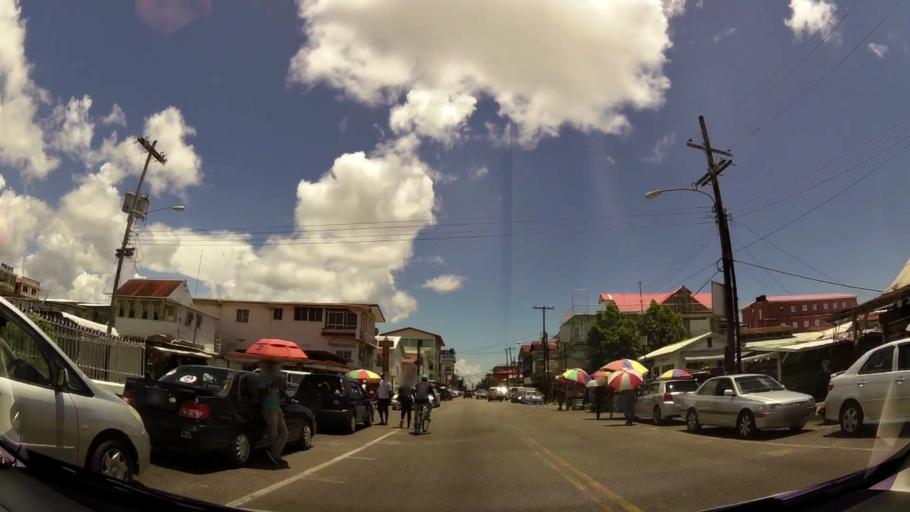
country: GY
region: Demerara-Mahaica
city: Georgetown
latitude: 6.8096
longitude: -58.1583
